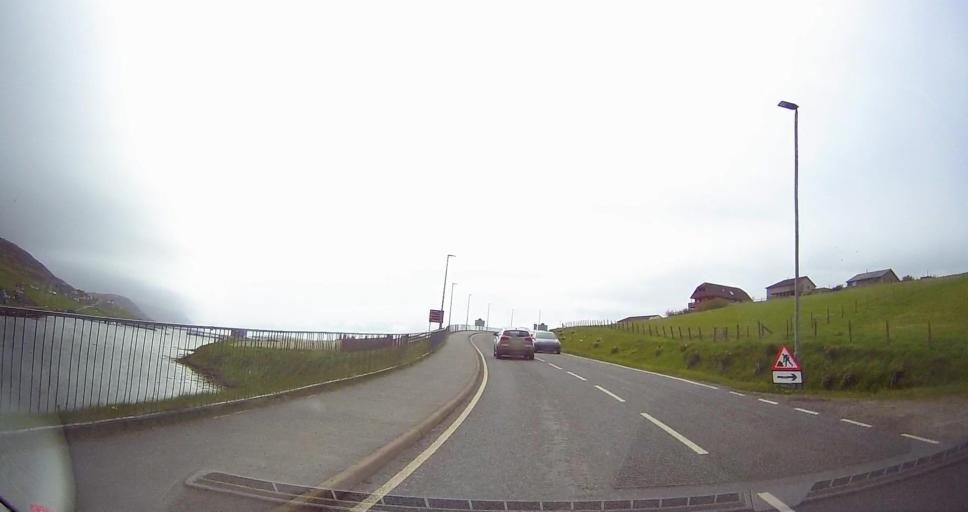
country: GB
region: Scotland
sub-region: Shetland Islands
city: Lerwick
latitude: 60.1423
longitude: -1.2672
